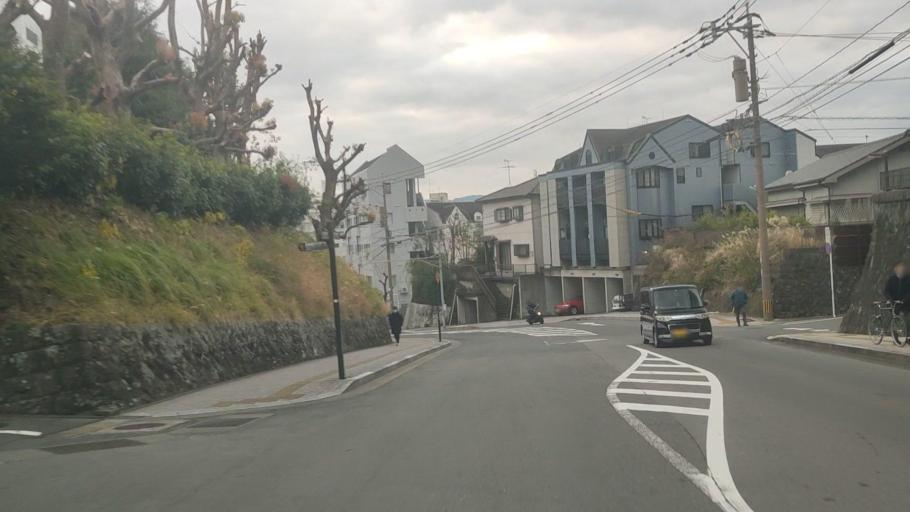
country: JP
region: Nagasaki
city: Nagasaki-shi
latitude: 32.7721
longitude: 129.8672
